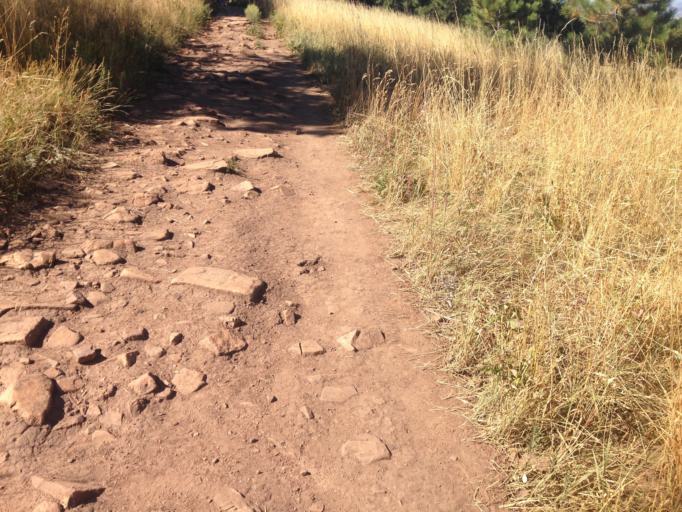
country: US
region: Colorado
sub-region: Boulder County
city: Boulder
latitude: 39.9807
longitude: -105.2841
